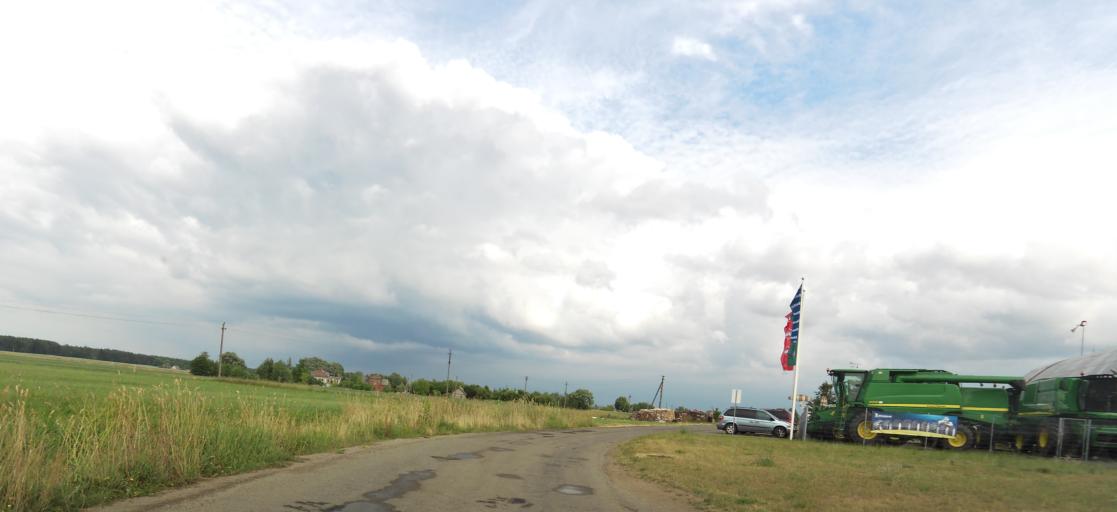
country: LT
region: Panevezys
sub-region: Panevezys City
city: Panevezys
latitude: 55.8290
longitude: 24.3590
